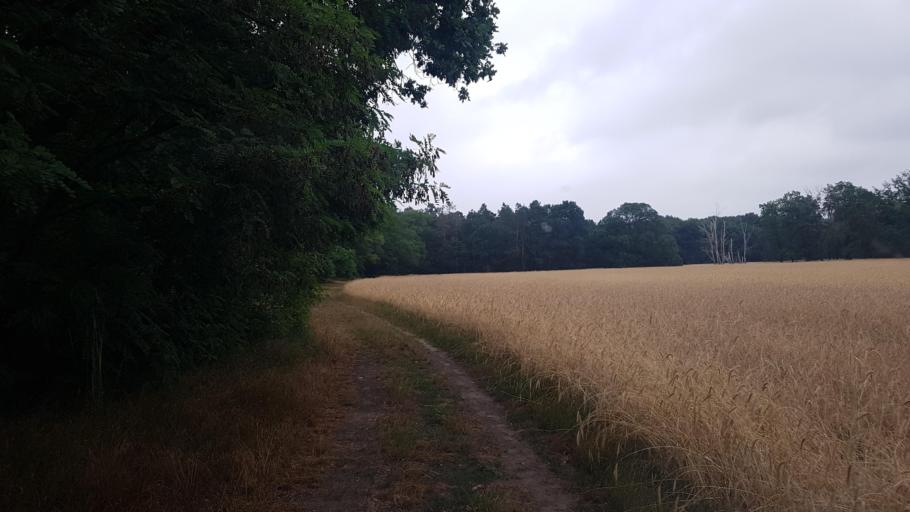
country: DE
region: Brandenburg
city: Ludwigsfelde
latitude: 52.2782
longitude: 13.3011
